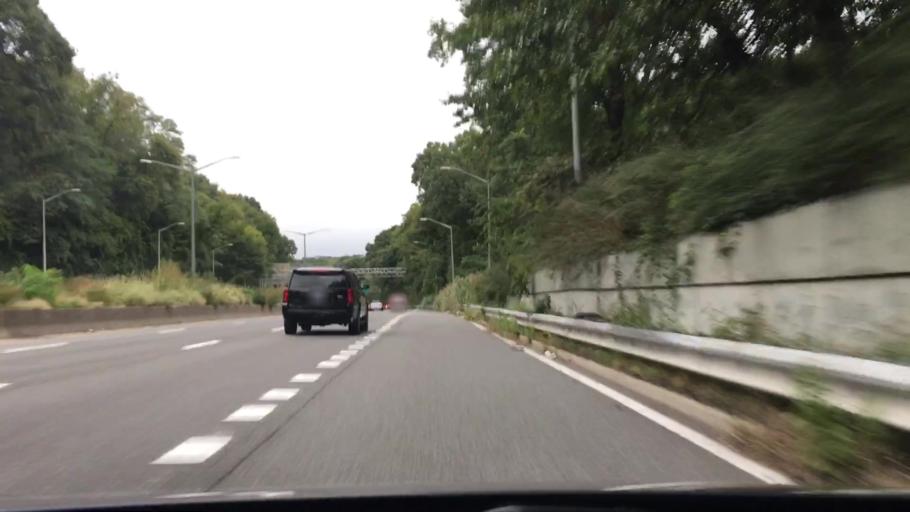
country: US
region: New York
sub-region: Nassau County
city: Bellerose Terrace
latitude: 40.7466
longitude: -73.7361
